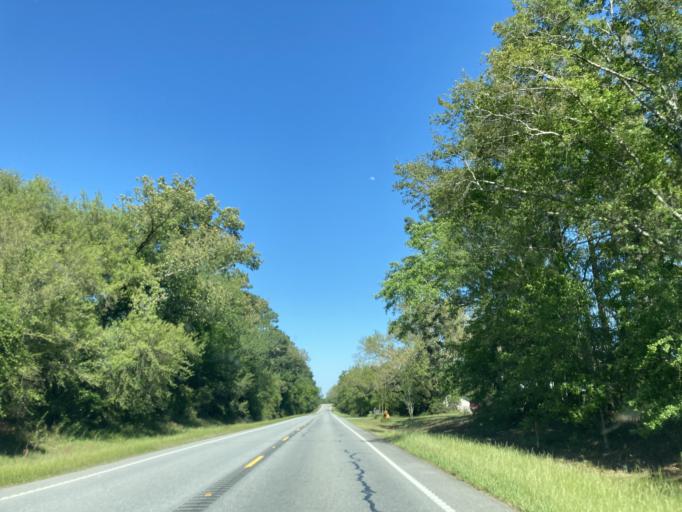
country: US
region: Georgia
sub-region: Miller County
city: Colquitt
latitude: 31.1868
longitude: -84.5292
